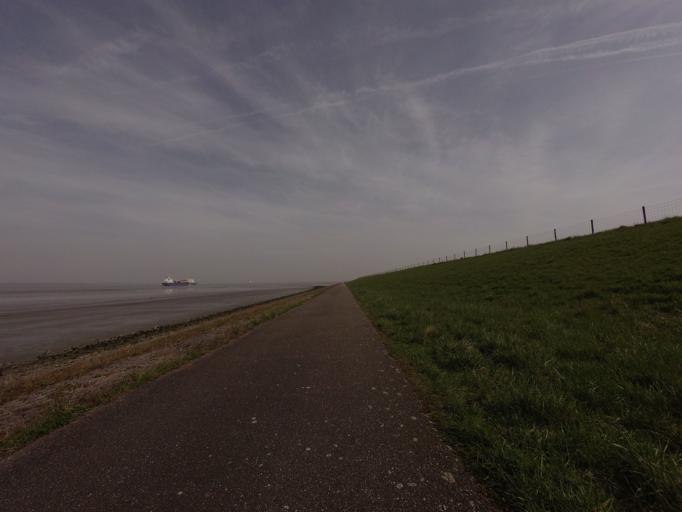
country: NL
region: Zeeland
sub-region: Gemeente Hulst
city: Hulst
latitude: 51.3641
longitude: 4.0814
